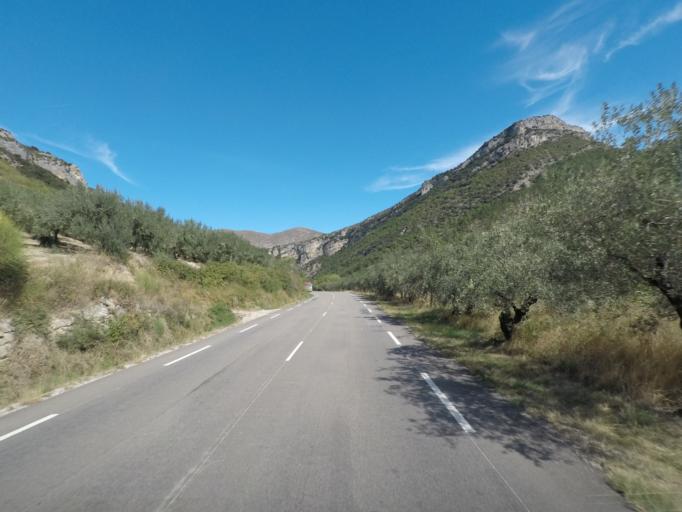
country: FR
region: Rhone-Alpes
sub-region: Departement de la Drome
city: Buis-les-Baronnies
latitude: 44.4207
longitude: 5.2747
